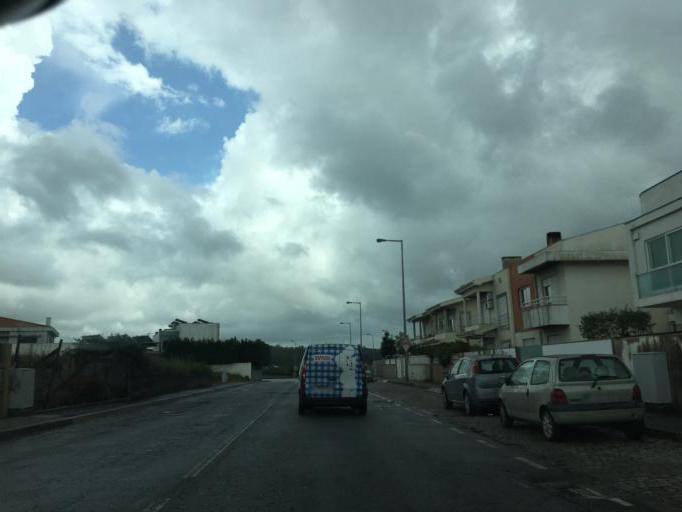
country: PT
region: Porto
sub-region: Maia
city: Nogueira
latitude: 41.2538
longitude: -8.5933
